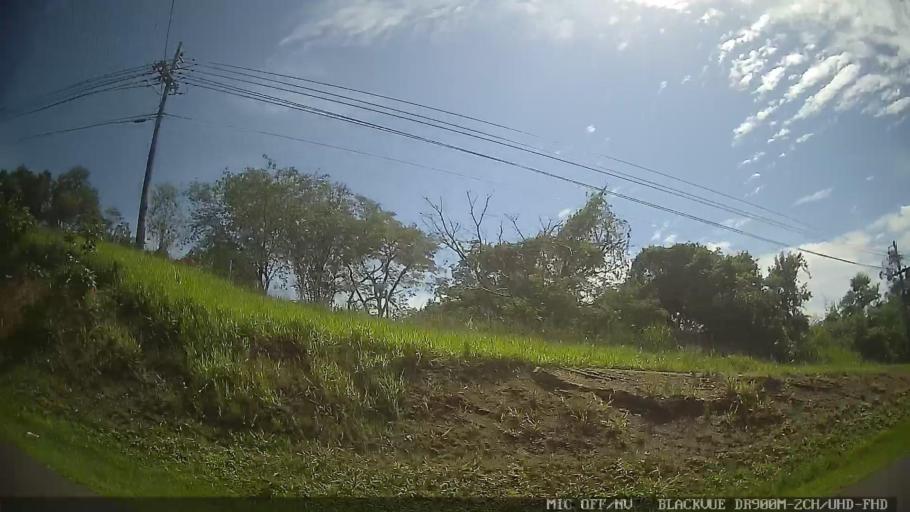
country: BR
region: Sao Paulo
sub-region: Porto Feliz
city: Porto Feliz
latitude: -23.2263
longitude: -47.5687
